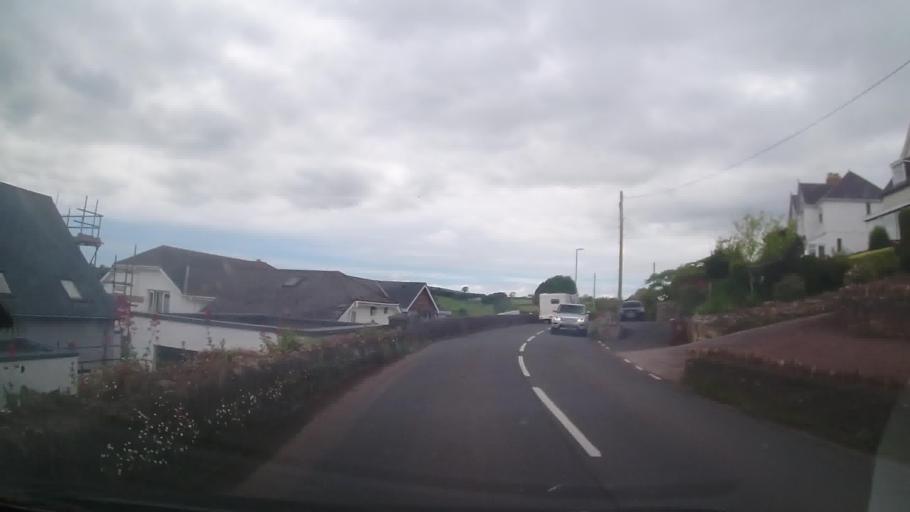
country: GB
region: England
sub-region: Devon
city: Kingsbridge
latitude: 50.2727
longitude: -3.7679
